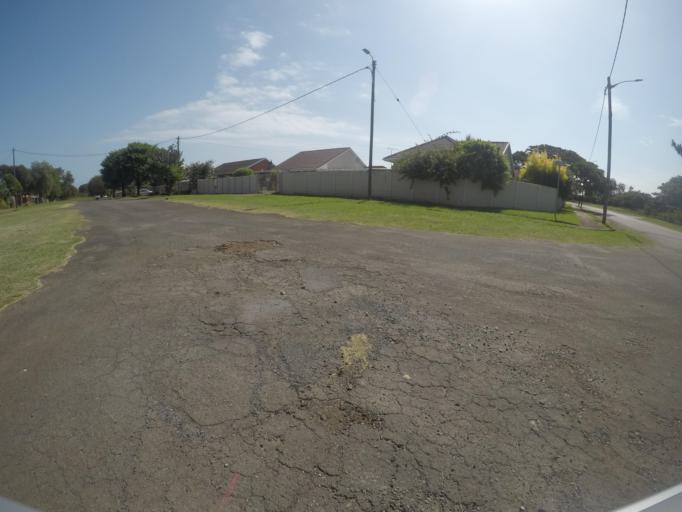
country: ZA
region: Eastern Cape
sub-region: Buffalo City Metropolitan Municipality
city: East London
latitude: -32.9684
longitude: 27.8773
